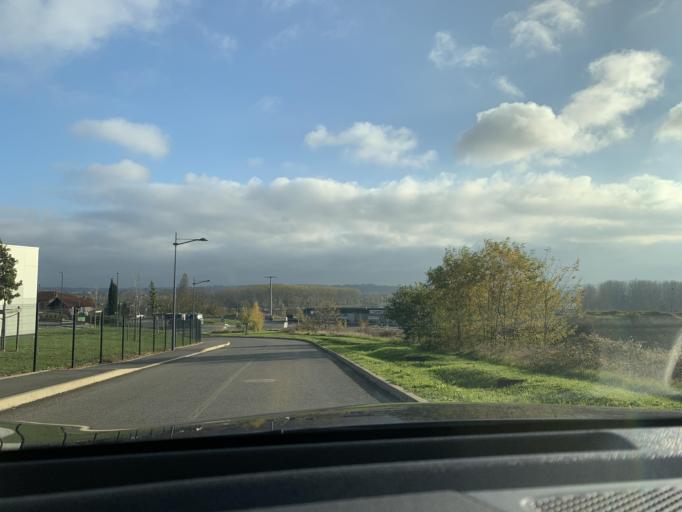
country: FR
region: Rhone-Alpes
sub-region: Departement du Rhone
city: Pommiers
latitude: 45.9593
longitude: 4.7137
